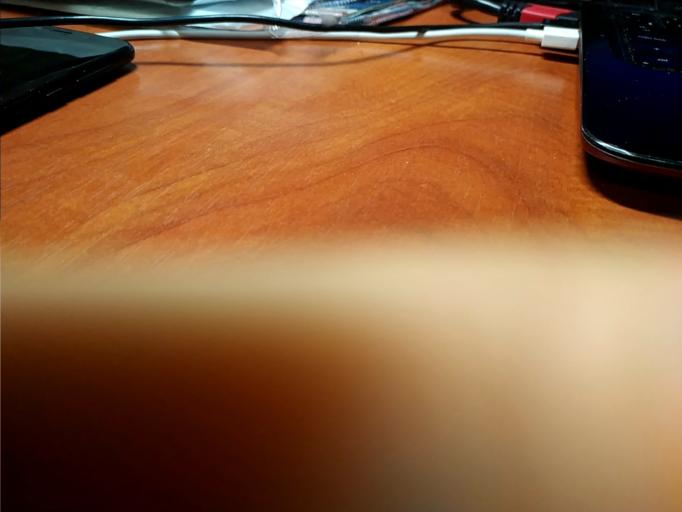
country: RU
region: Tverskaya
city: Maksatikha
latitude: 57.6031
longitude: 35.8181
